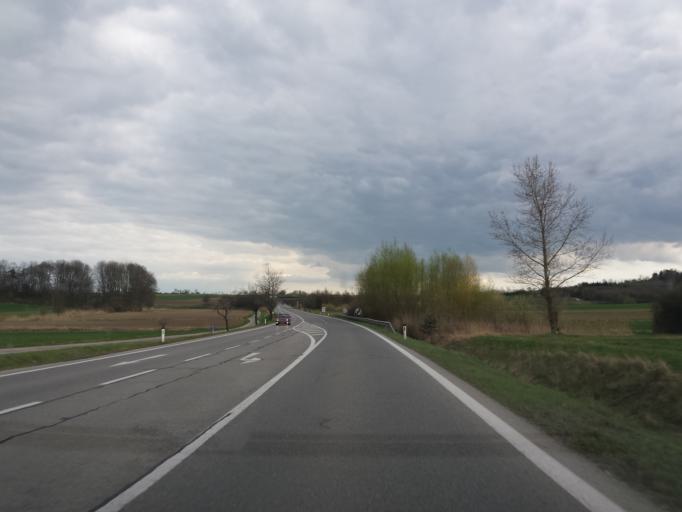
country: AT
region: Lower Austria
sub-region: Politischer Bezirk Krems
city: Lengenfeld
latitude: 48.4691
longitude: 15.5817
